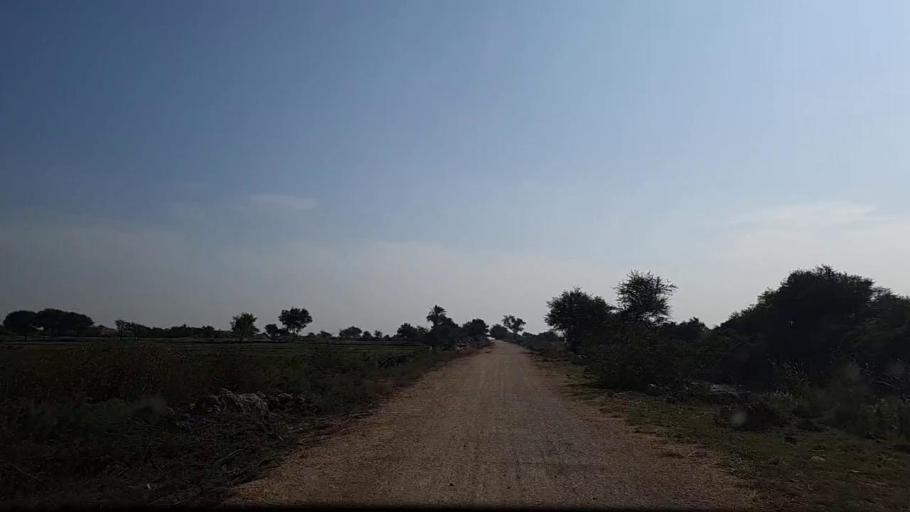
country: PK
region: Sindh
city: Daro Mehar
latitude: 24.7211
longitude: 68.1157
